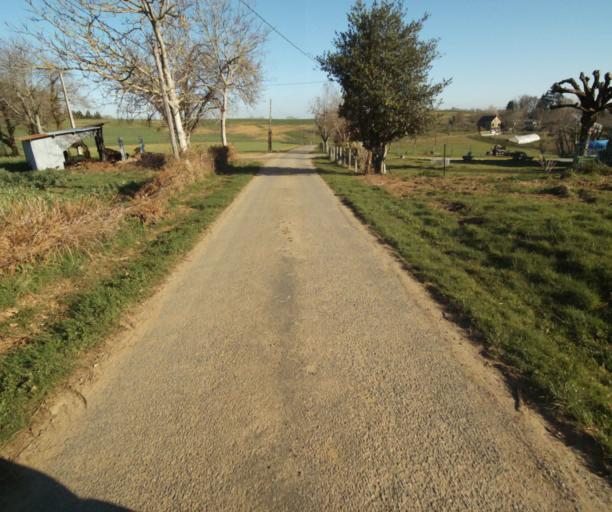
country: FR
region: Limousin
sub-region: Departement de la Correze
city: Uzerche
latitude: 45.3907
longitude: 1.6195
